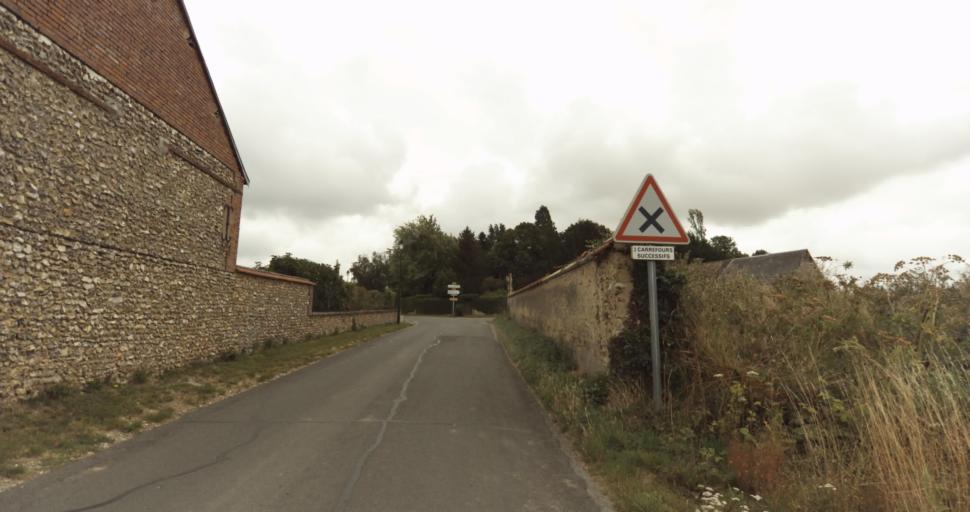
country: FR
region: Haute-Normandie
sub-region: Departement de l'Eure
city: La Couture-Boussey
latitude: 48.9464
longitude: 1.3630
